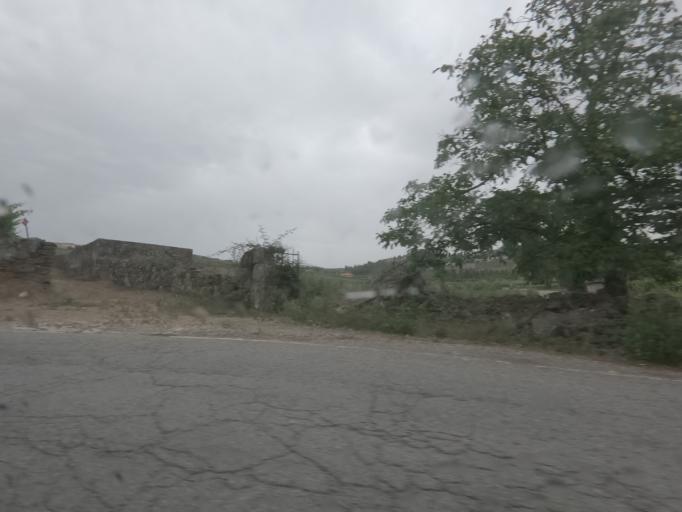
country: PT
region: Viseu
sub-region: Armamar
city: Armamar
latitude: 41.1148
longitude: -7.7250
